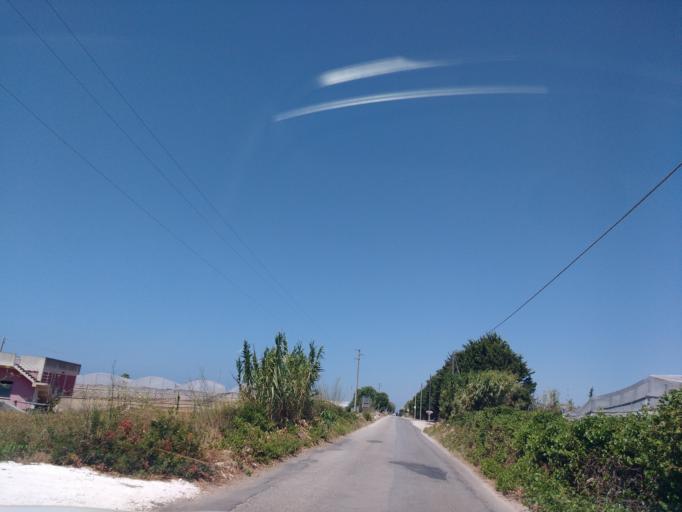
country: IT
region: Sicily
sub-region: Provincia di Siracusa
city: Pachino
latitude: 36.6735
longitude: 15.0898
